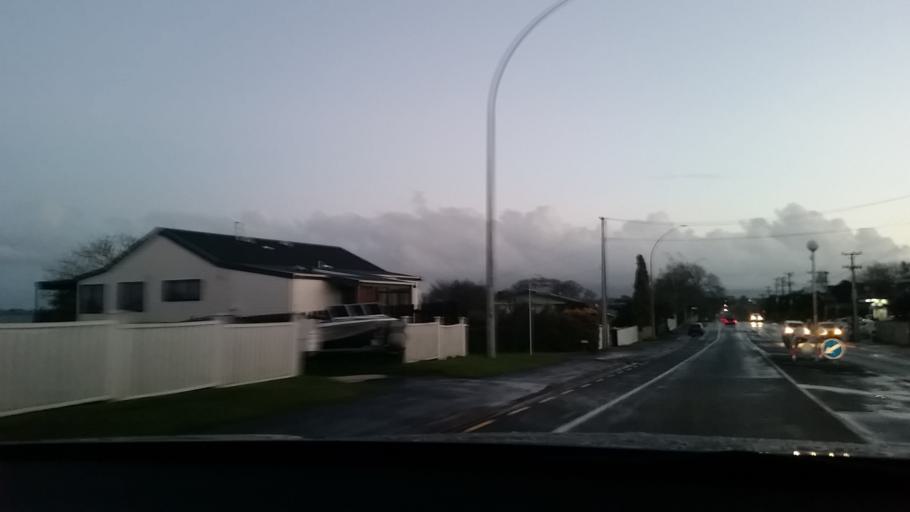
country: NZ
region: Waikato
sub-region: Hamilton City
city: Hamilton
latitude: -37.8025
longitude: 175.2450
